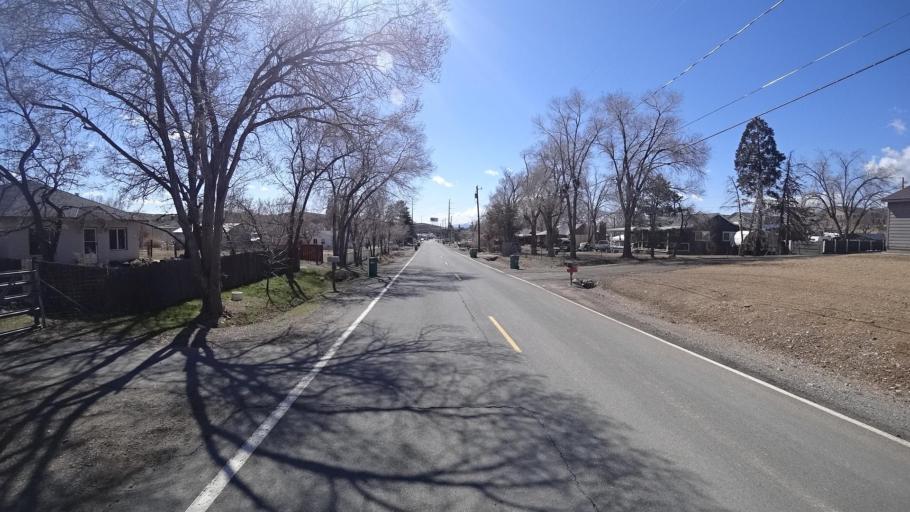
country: US
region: Nevada
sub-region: Washoe County
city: Golden Valley
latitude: 39.5912
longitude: -119.8224
